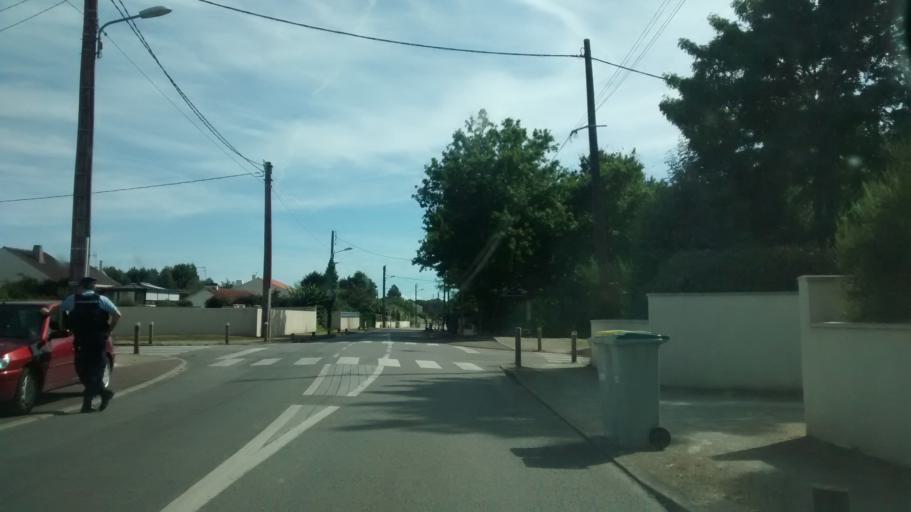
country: FR
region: Pays de la Loire
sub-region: Departement de la Loire-Atlantique
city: Pont-Saint-Martin
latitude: 47.1284
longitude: -1.6164
